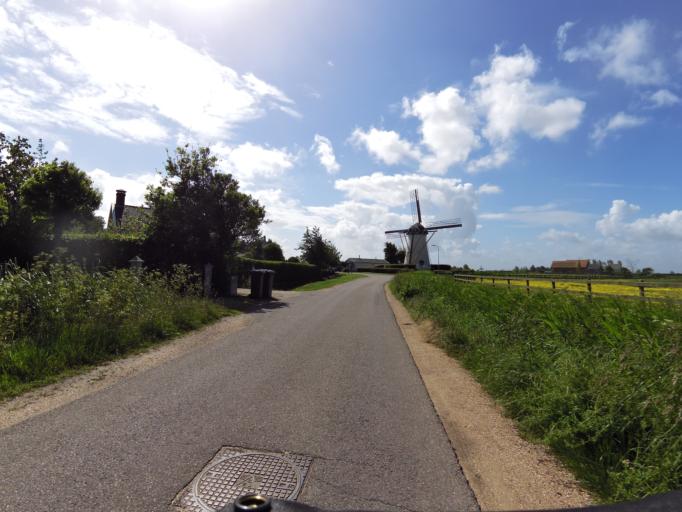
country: NL
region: Zeeland
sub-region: Schouwen-Duiveland
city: Bruinisse
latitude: 51.6885
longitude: 3.9868
